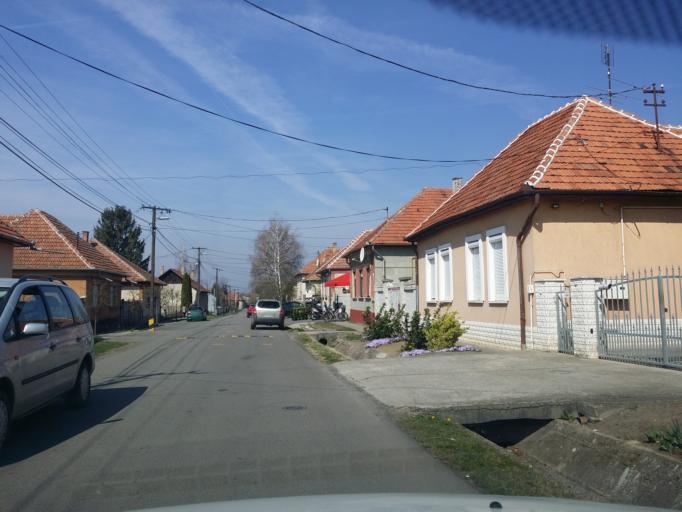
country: HU
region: Pest
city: Cegledbercel
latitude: 47.2169
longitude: 19.6802
